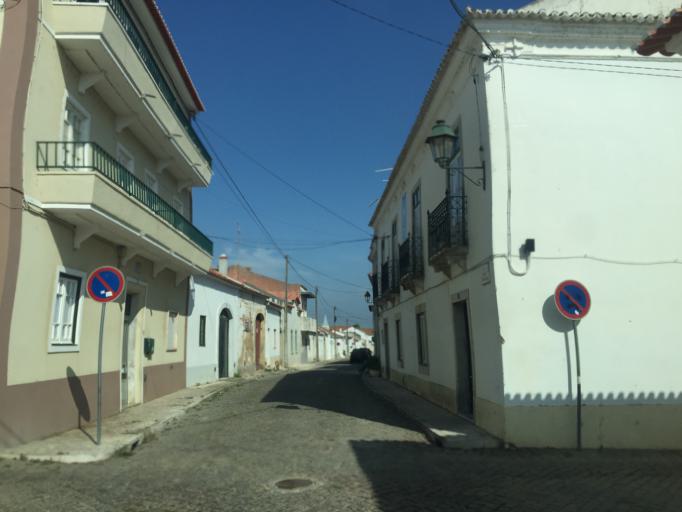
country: PT
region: Santarem
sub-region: Salvaterra de Magos
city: Salvaterra de Magos
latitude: 39.0295
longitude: -8.7918
